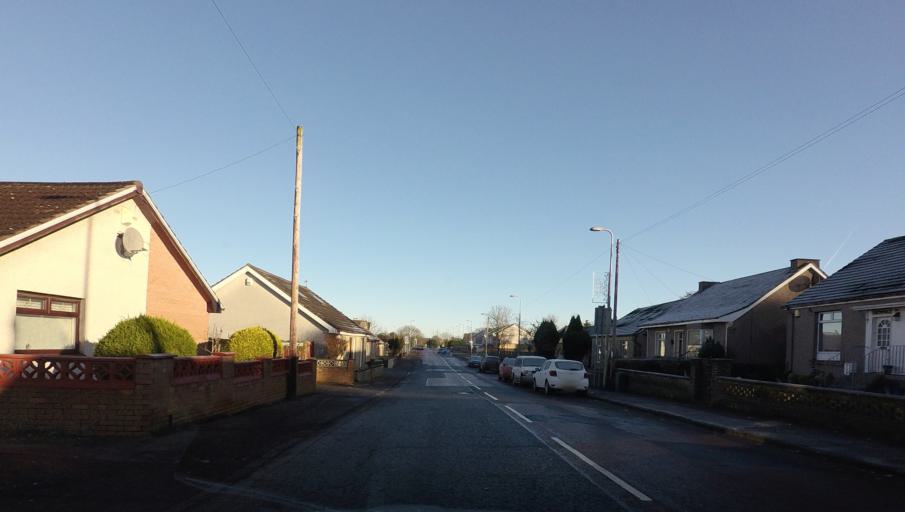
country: GB
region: Scotland
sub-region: North Lanarkshire
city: Newmains
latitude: 55.7853
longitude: -3.8728
